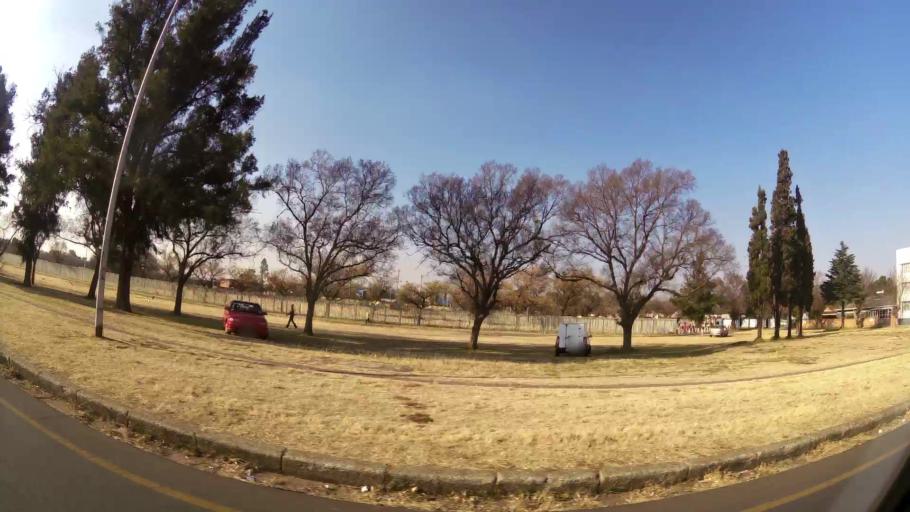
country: ZA
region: Gauteng
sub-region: Ekurhuleni Metropolitan Municipality
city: Brakpan
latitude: -26.2342
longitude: 28.3633
